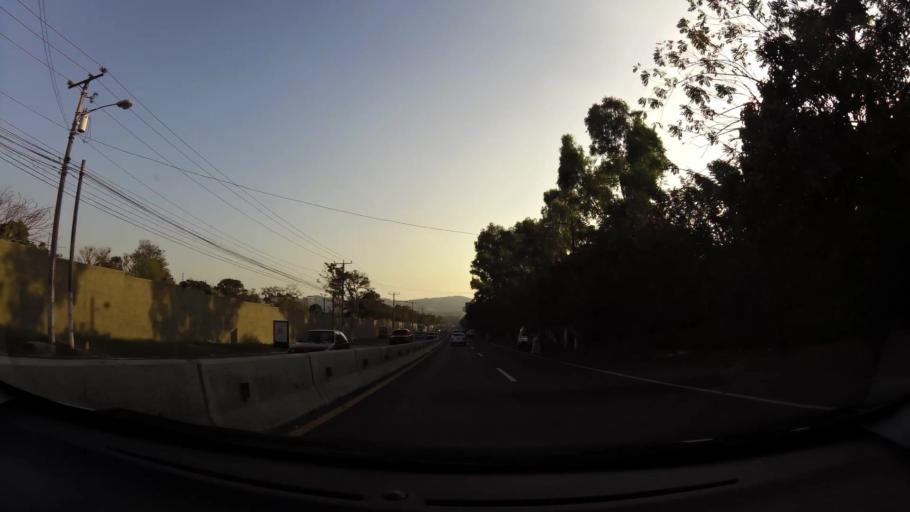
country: SV
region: La Libertad
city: Antiguo Cuscatlan
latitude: 13.6937
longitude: -89.2503
